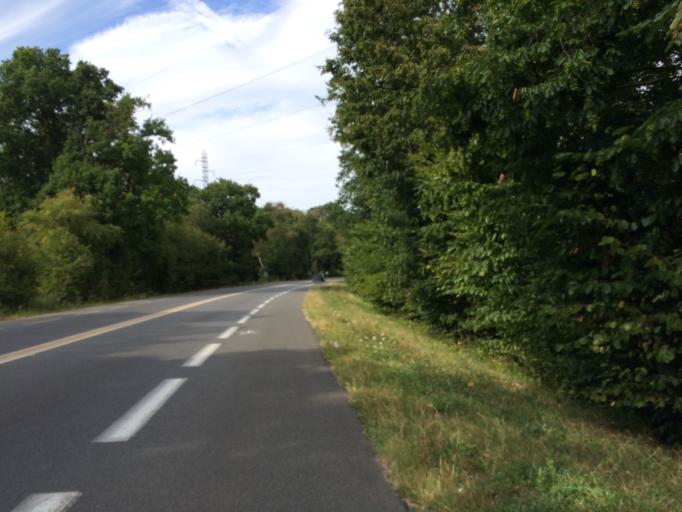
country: FR
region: Ile-de-France
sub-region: Departement de l'Essonne
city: Quincy-sous-Senart
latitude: 48.6745
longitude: 2.5248
